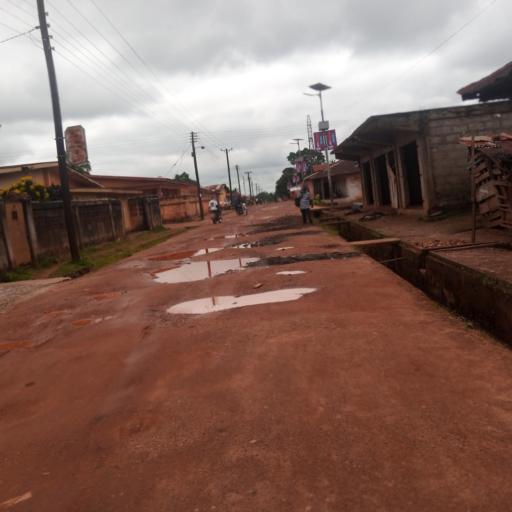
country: SL
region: Eastern Province
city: Kenema
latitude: 7.8845
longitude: -11.1861
